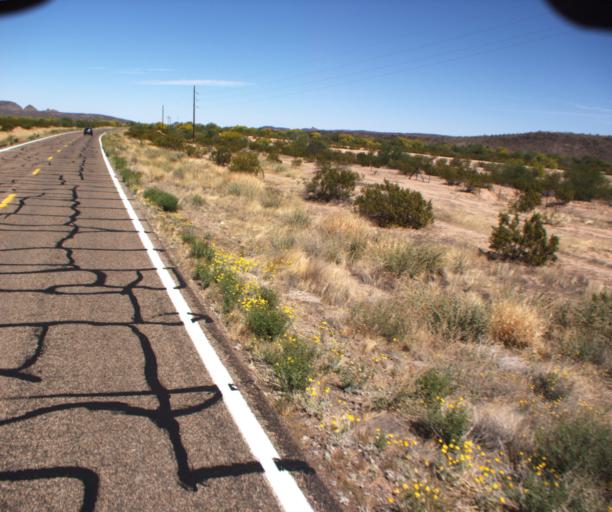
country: US
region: Arizona
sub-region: Pima County
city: Ajo
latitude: 32.4922
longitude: -112.8817
